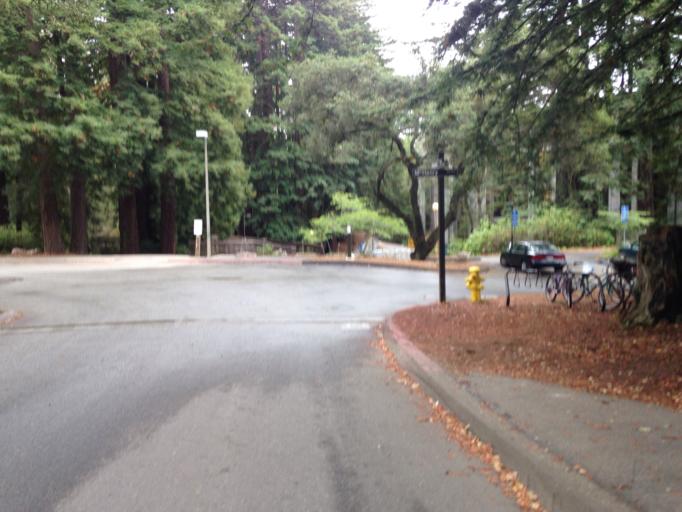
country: US
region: California
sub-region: Santa Cruz County
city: Pasatiempo
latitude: 36.9966
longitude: -122.0590
